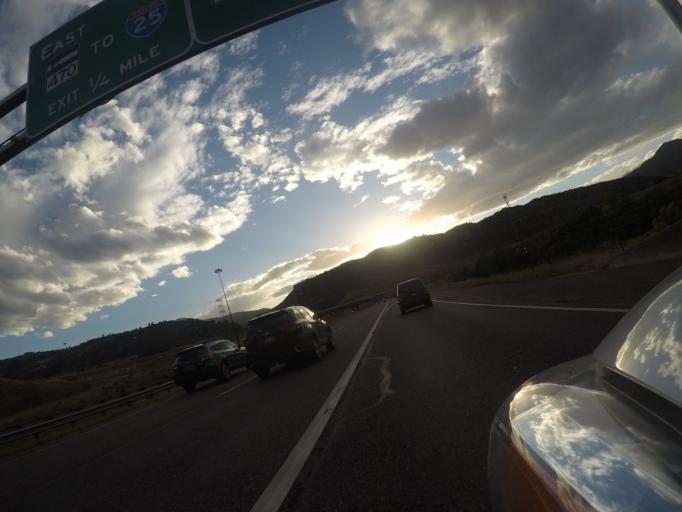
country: US
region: Colorado
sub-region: Jefferson County
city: Ken Caryl
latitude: 39.6381
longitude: -105.1610
